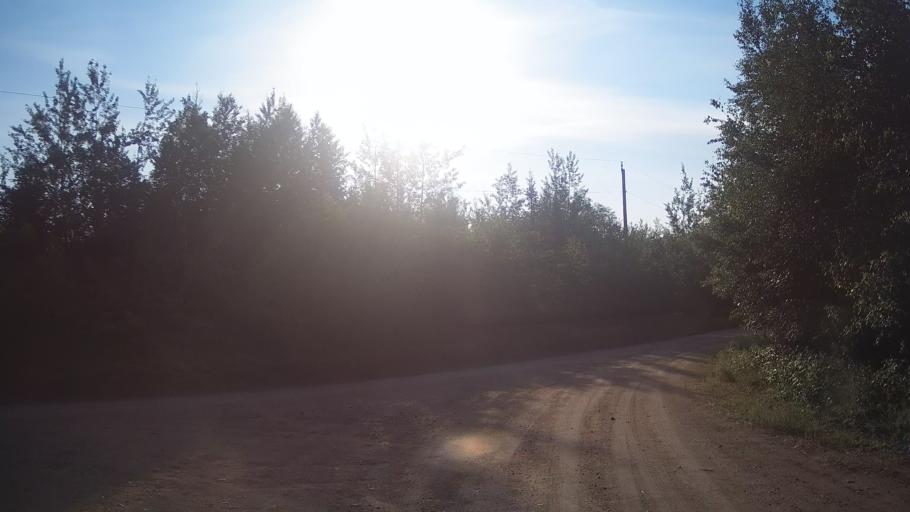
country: CA
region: Ontario
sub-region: Rainy River District
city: Atikokan
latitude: 49.4039
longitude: -91.6254
